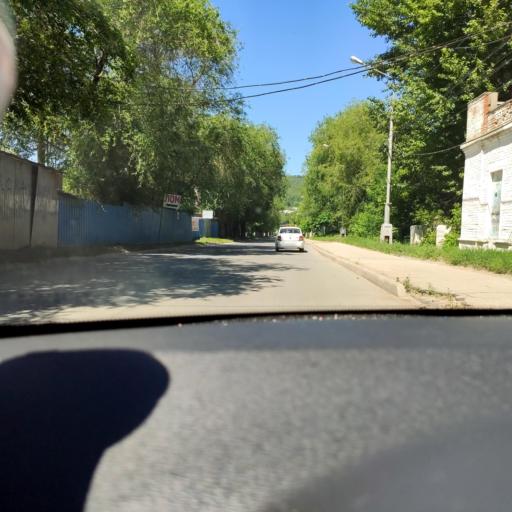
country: RU
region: Samara
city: Volzhskiy
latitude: 53.3833
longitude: 50.1719
